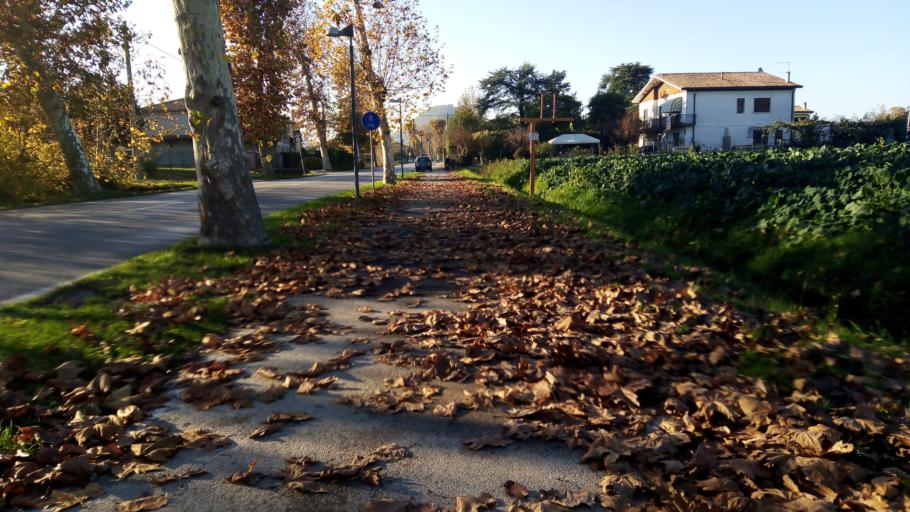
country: IT
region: Veneto
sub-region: Provincia di Padova
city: Abano Terme
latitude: 45.3631
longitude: 11.7773
